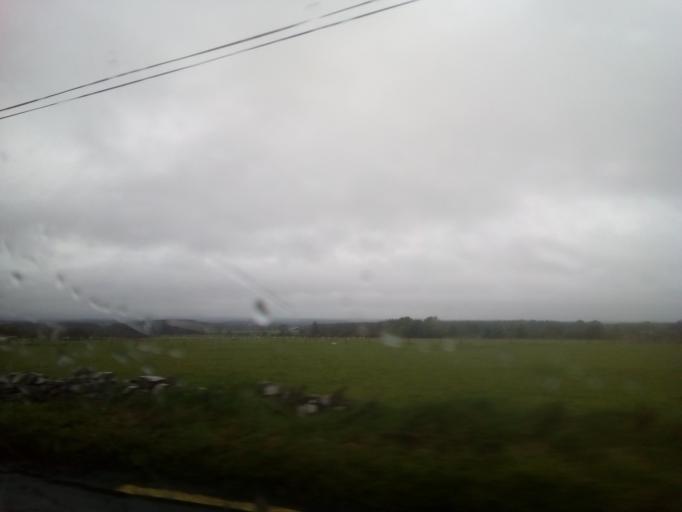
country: IE
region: Connaught
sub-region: Roscommon
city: Boyle
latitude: 53.8221
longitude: -8.3527
